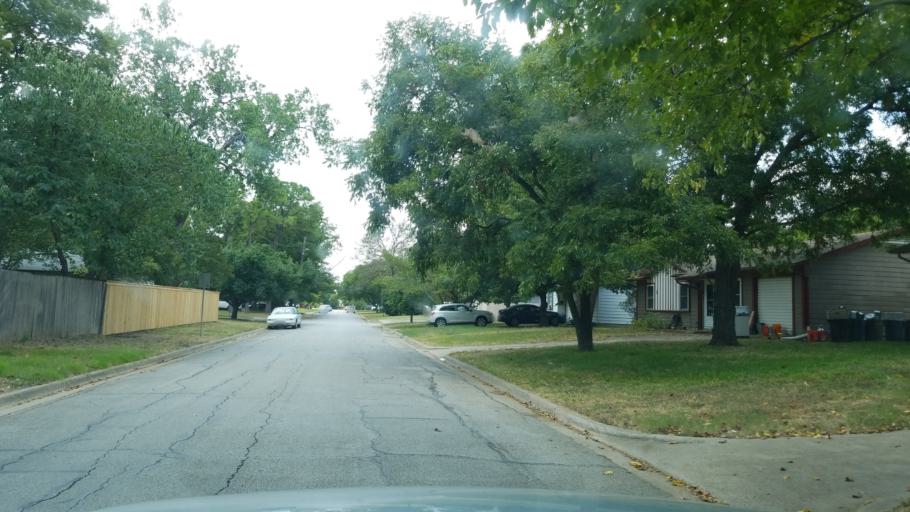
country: US
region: Texas
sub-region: Tarrant County
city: Euless
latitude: 32.8494
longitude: -97.0854
